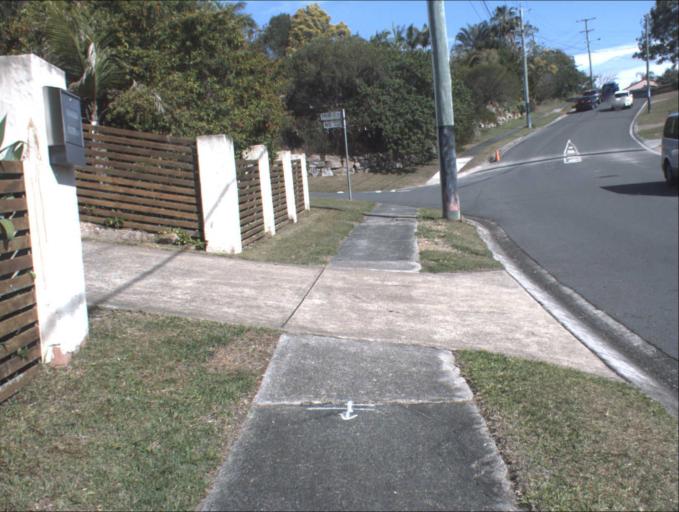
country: AU
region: Queensland
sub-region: Logan
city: Slacks Creek
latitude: -27.6500
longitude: 153.1812
